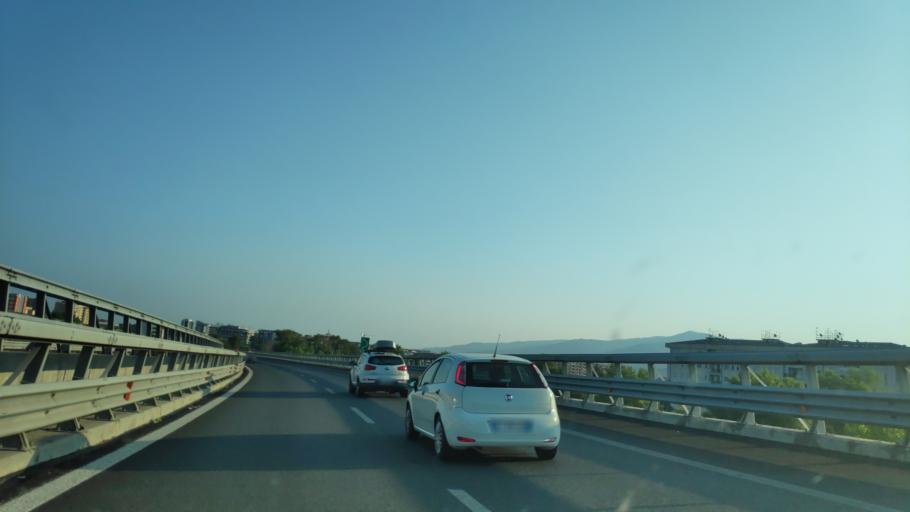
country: IT
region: Calabria
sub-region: Provincia di Cosenza
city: Cosenza
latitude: 39.3165
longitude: 16.2416
